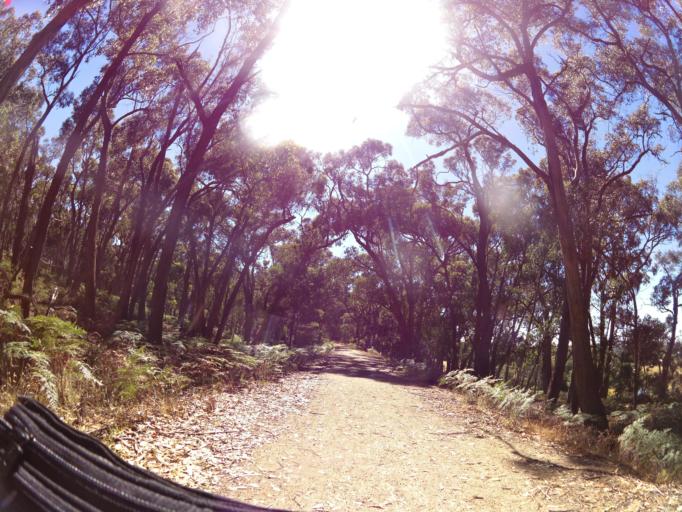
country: AU
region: Victoria
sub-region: Ballarat North
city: Delacombe
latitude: -37.6741
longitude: 143.5315
